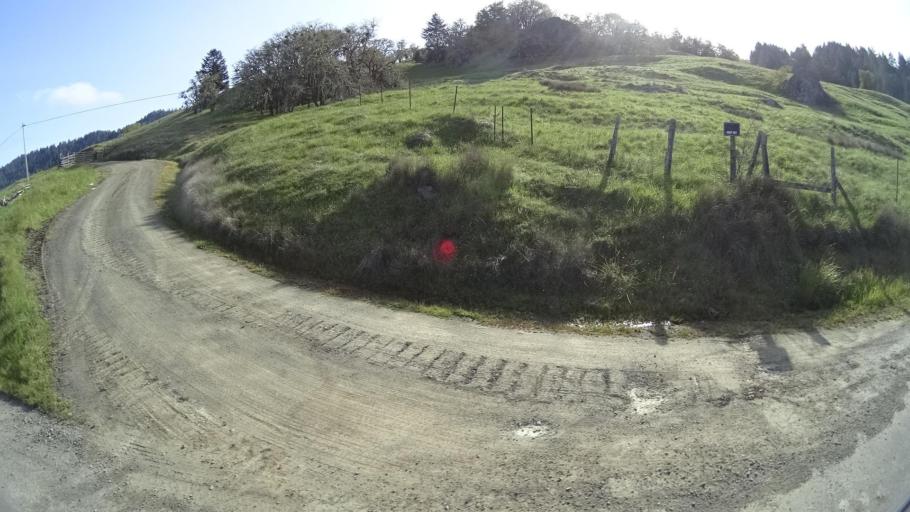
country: US
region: California
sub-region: Humboldt County
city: Hydesville
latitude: 40.6574
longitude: -123.9257
